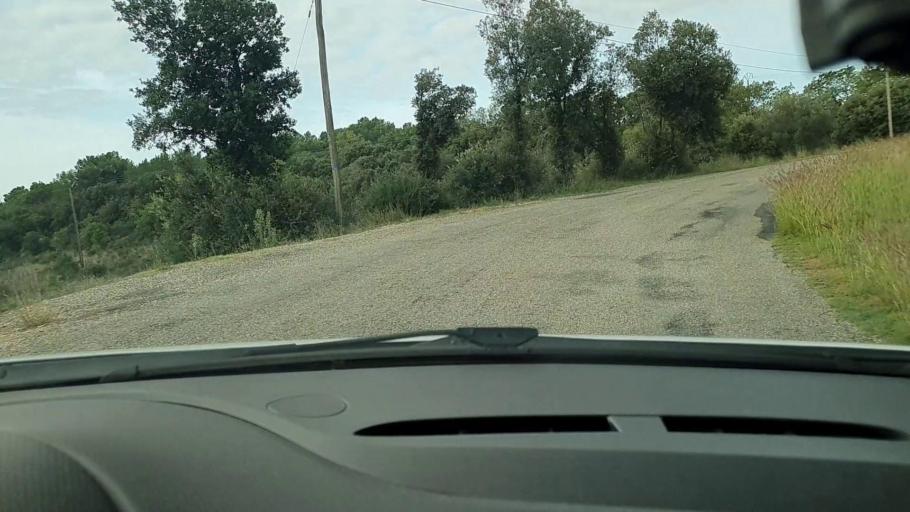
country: FR
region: Languedoc-Roussillon
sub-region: Departement du Gard
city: Montaren-et-Saint-Mediers
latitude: 44.0874
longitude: 4.2954
